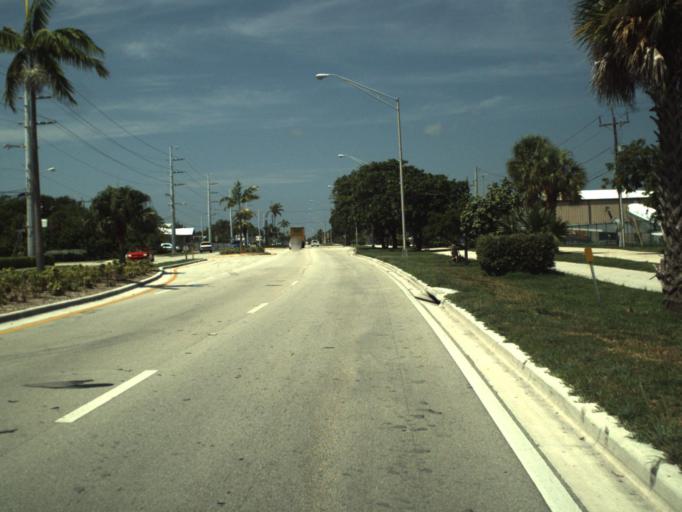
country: US
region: Florida
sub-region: Monroe County
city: Marathon
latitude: 24.7278
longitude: -81.0425
